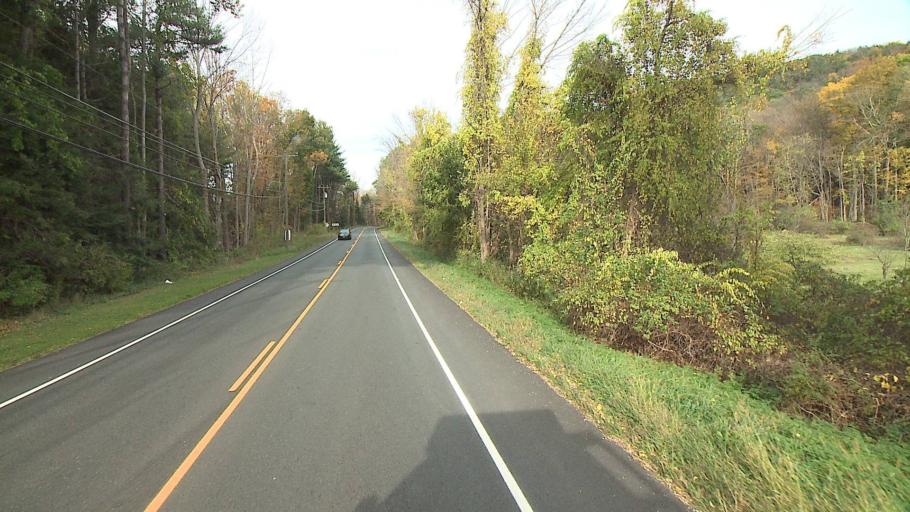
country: US
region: Connecticut
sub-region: Litchfield County
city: Canaan
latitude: 41.9921
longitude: -73.4150
